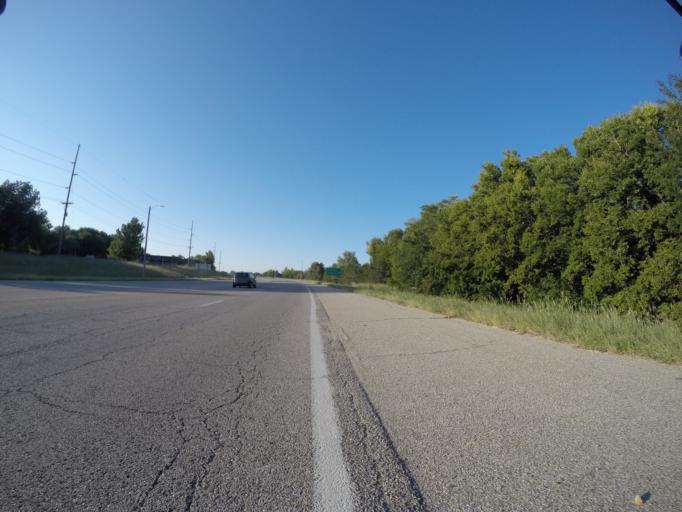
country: US
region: Kansas
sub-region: Riley County
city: Manhattan
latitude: 39.1977
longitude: -96.6124
